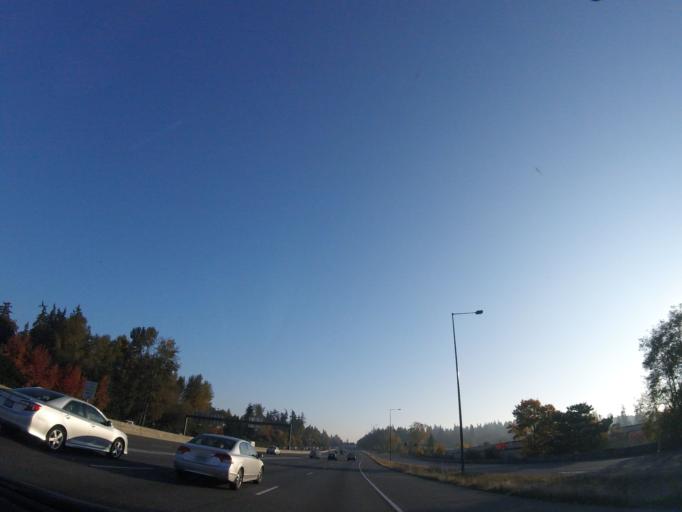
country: US
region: Washington
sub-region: King County
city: Kingsgate
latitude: 47.7018
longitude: -122.1799
